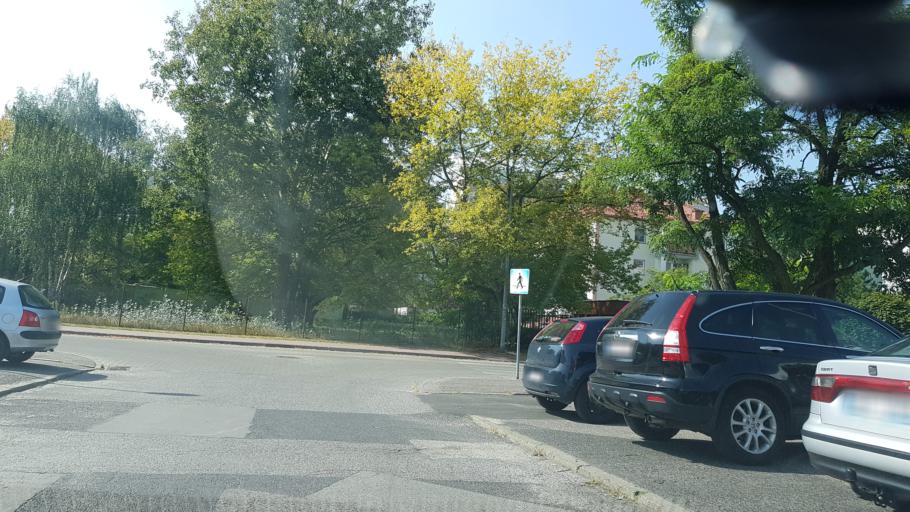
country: PL
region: Masovian Voivodeship
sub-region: Warszawa
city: Bielany
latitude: 52.2749
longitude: 20.9219
